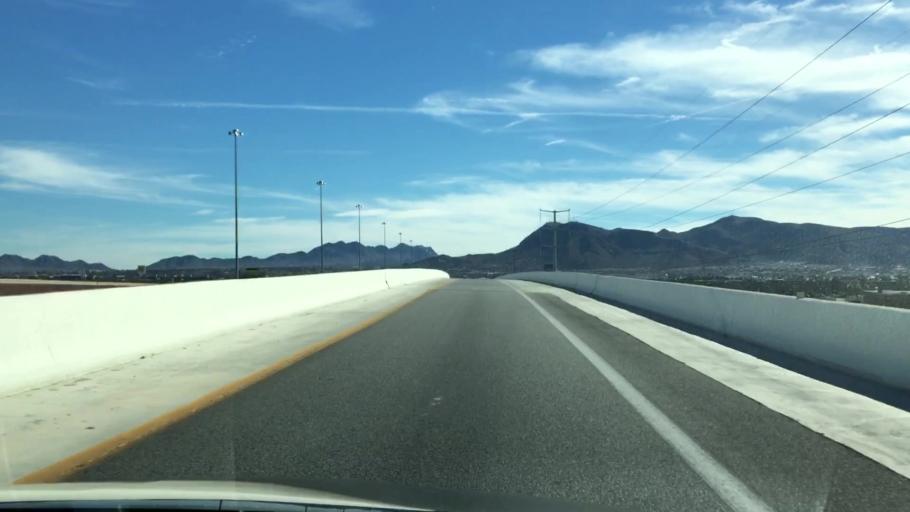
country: US
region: Nevada
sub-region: Clark County
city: Whitney
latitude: 36.0666
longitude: -115.0341
